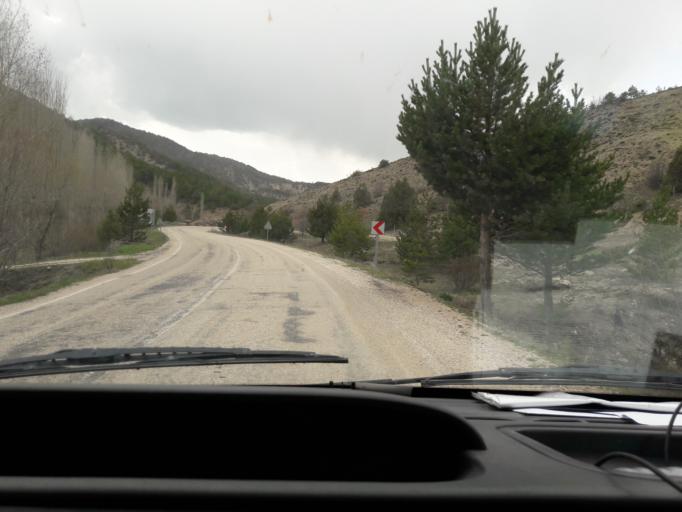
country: TR
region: Giresun
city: Alucra
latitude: 40.2749
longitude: 38.8308
